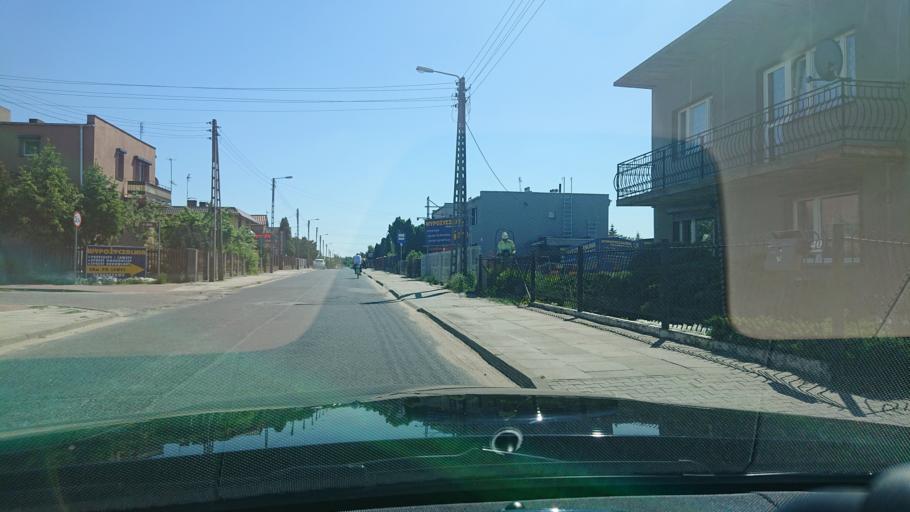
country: PL
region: Greater Poland Voivodeship
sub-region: Powiat gnieznienski
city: Gniezno
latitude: 52.5082
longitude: 17.5888
